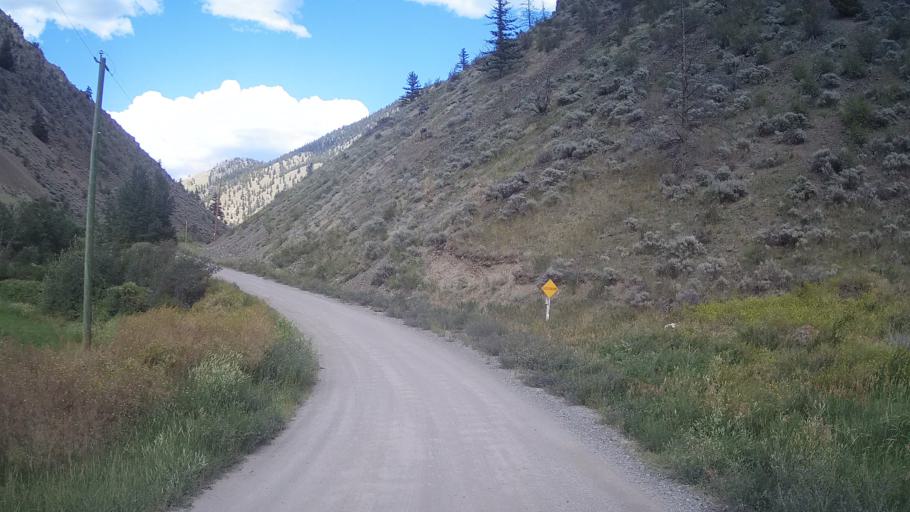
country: CA
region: British Columbia
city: Lillooet
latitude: 51.1959
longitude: -122.1131
